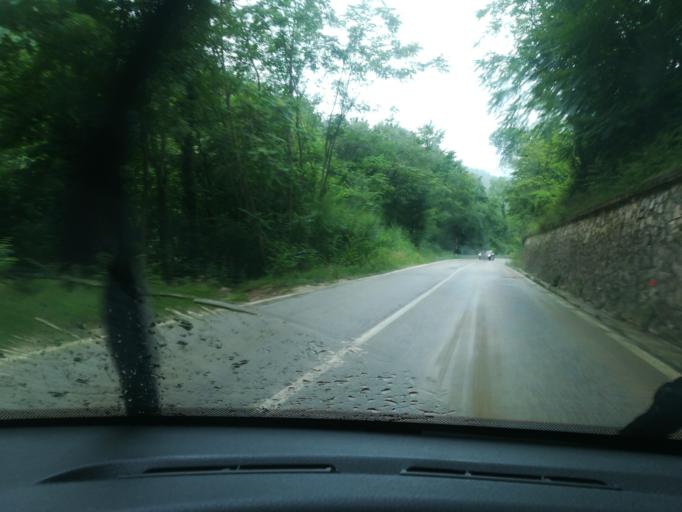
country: IT
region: The Marches
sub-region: Province of Fermo
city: Amandola
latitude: 42.9836
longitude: 13.3463
